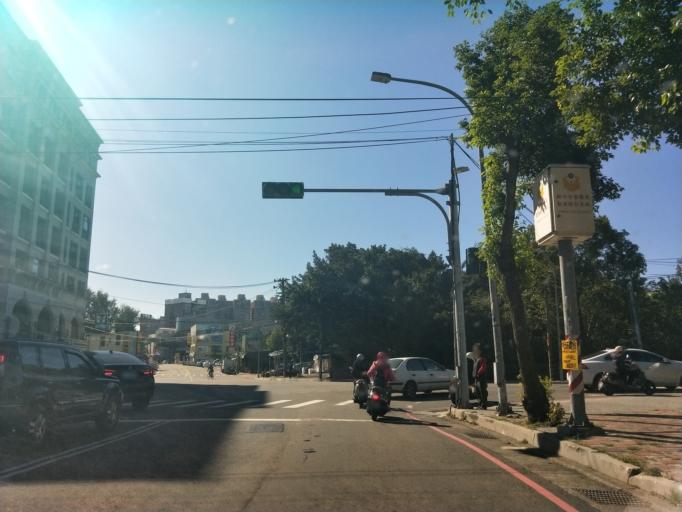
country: TW
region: Taiwan
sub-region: Hsinchu
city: Hsinchu
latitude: 24.7968
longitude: 121.0021
